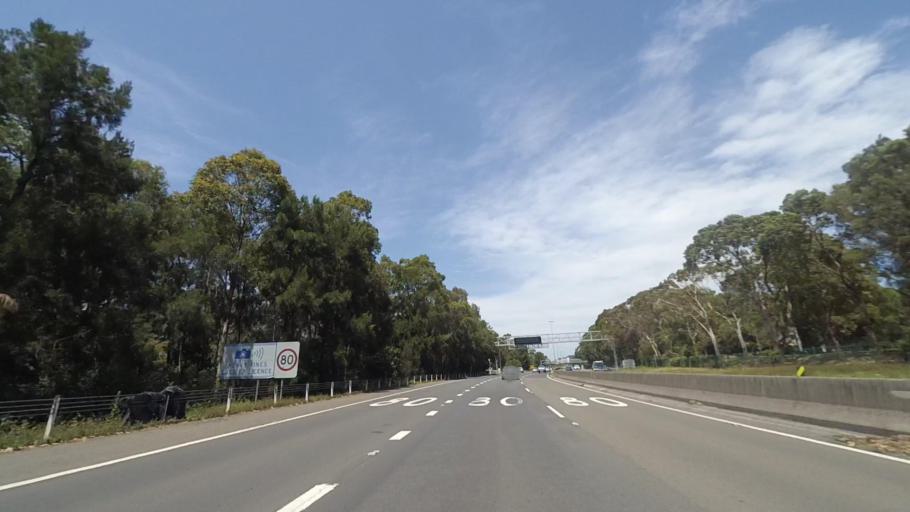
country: AU
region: New South Wales
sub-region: Wollongong
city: Mount Ousley
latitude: -34.4052
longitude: 150.8839
